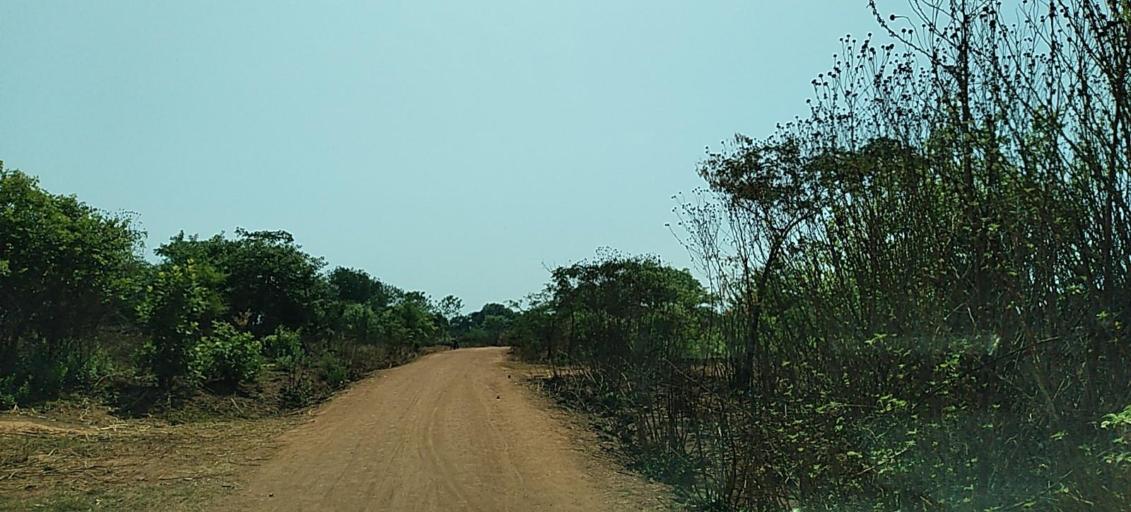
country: ZM
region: Copperbelt
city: Luanshya
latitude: -13.3484
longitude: 28.3964
